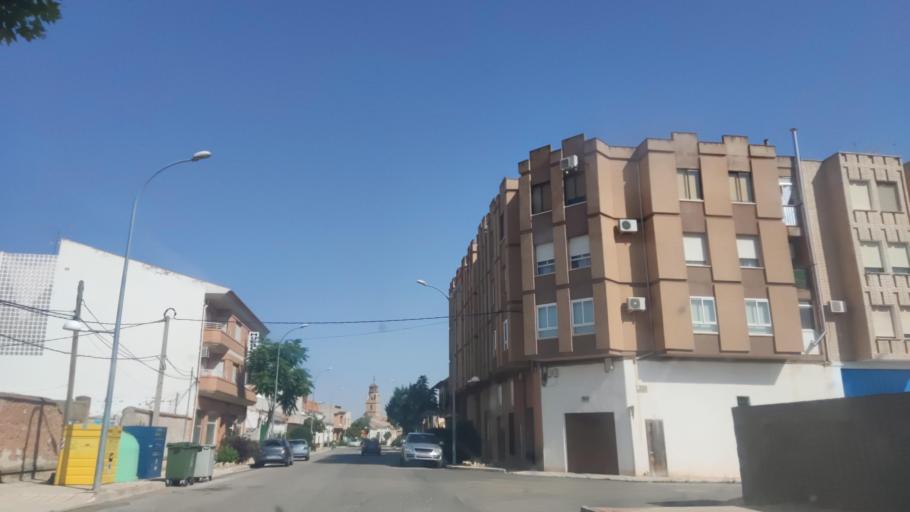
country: ES
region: Castille-La Mancha
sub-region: Provincia de Albacete
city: La Gineta
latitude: 39.1110
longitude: -1.9941
